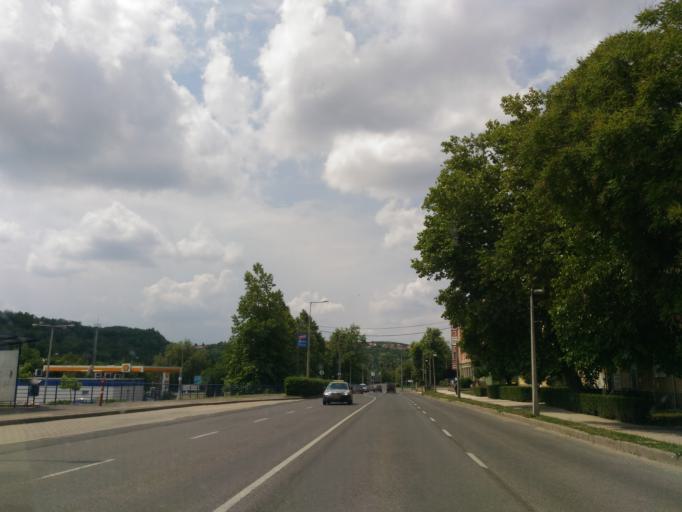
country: HU
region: Baranya
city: Komlo
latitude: 46.1925
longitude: 18.2581
